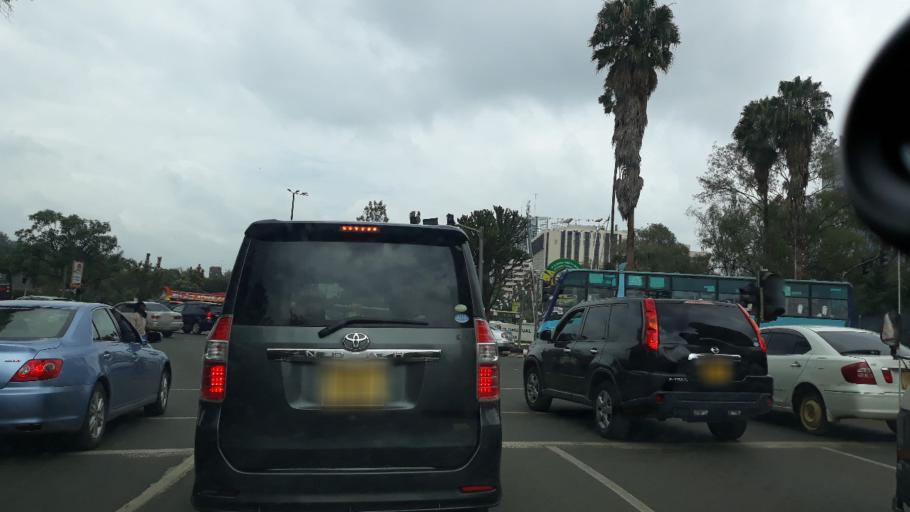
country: KE
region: Nairobi Area
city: Nairobi
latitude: -1.2870
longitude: 36.8175
